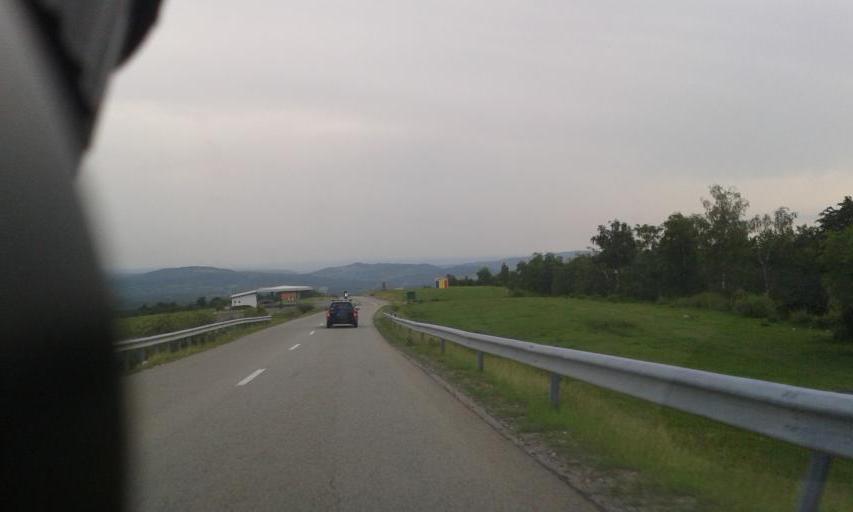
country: RO
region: Gorj
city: Novaci-Straini
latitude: 45.1983
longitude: 23.6895
